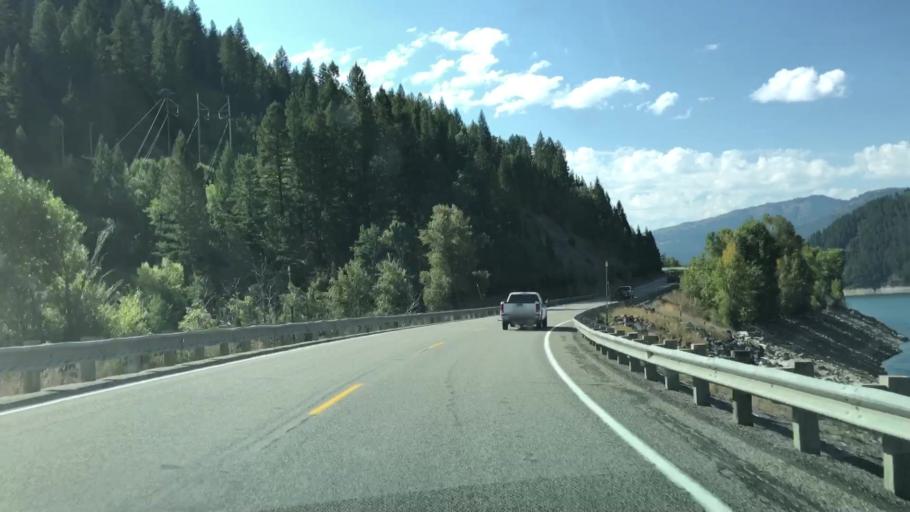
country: US
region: Idaho
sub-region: Teton County
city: Victor
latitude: 43.3179
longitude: -111.1448
